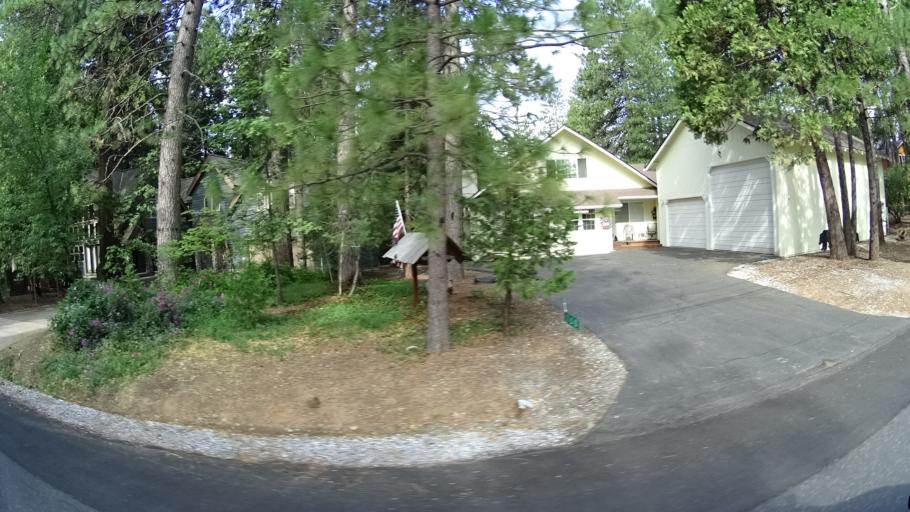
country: US
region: California
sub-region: Calaveras County
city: Arnold
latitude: 38.2629
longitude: -120.3342
